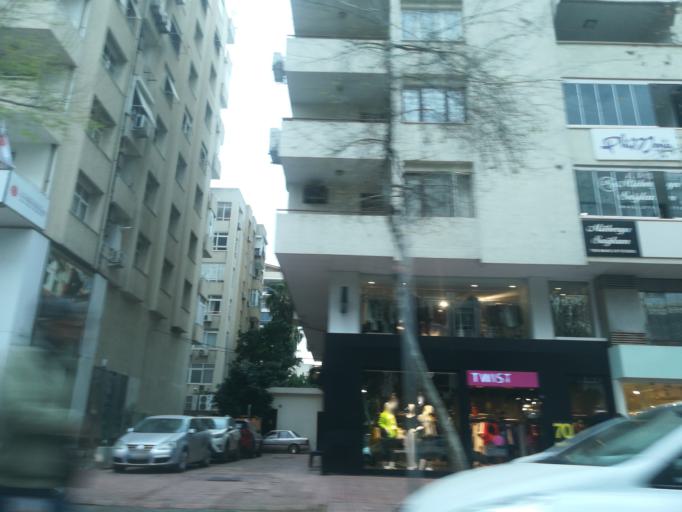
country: TR
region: Adana
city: Adana
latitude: 37.0009
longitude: 35.3203
